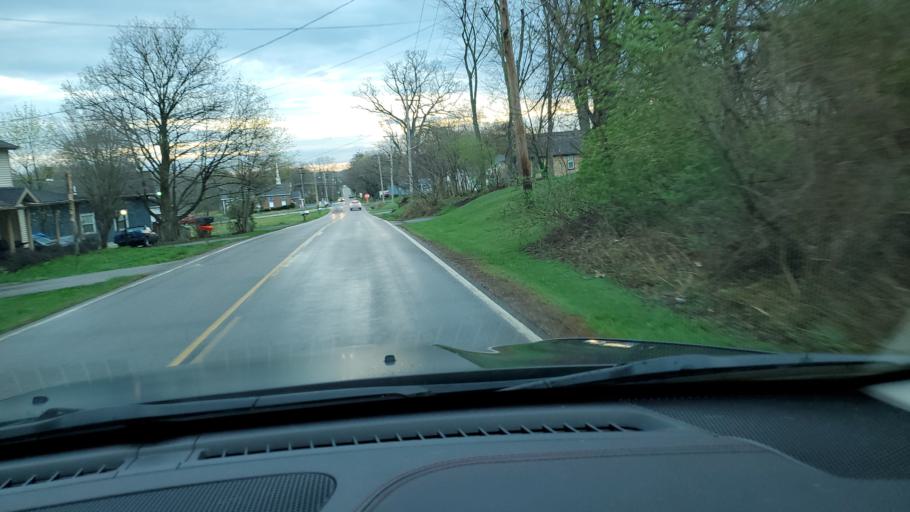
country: US
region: Ohio
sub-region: Trumbull County
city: Mineral Ridge
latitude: 41.1549
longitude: -80.7649
